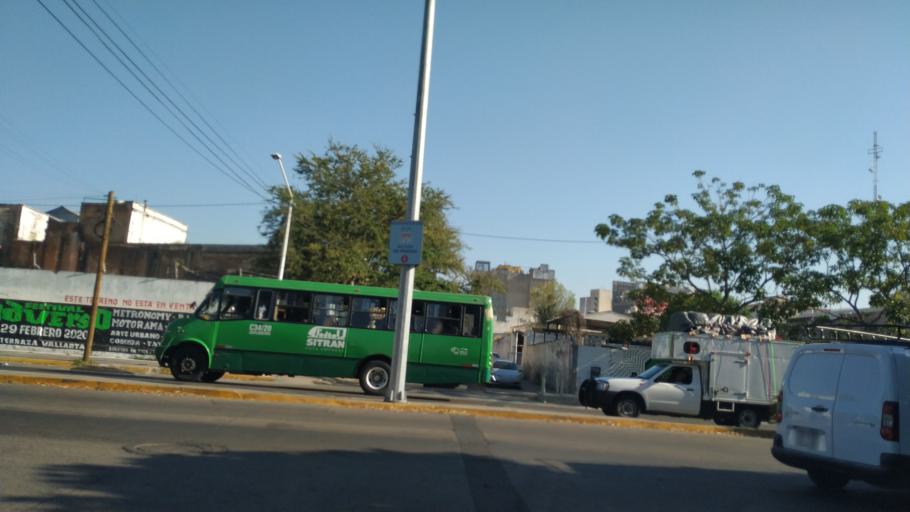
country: MX
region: Jalisco
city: Guadalajara
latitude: 20.6684
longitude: -103.3487
